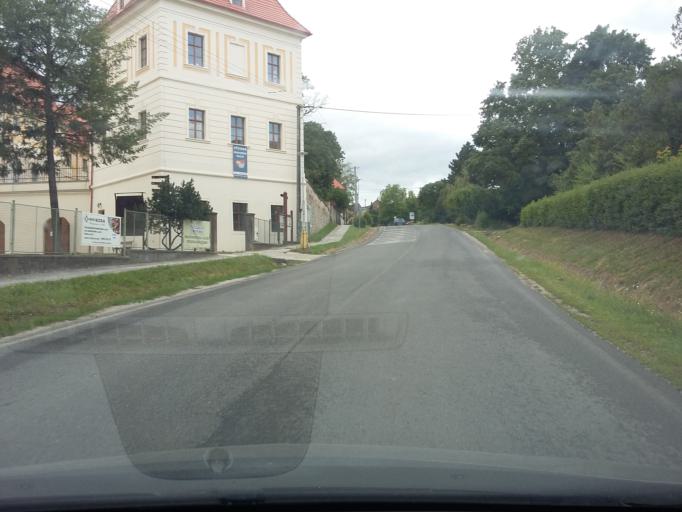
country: SK
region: Trnavsky
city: Vrbove
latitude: 48.5686
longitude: 17.6231
